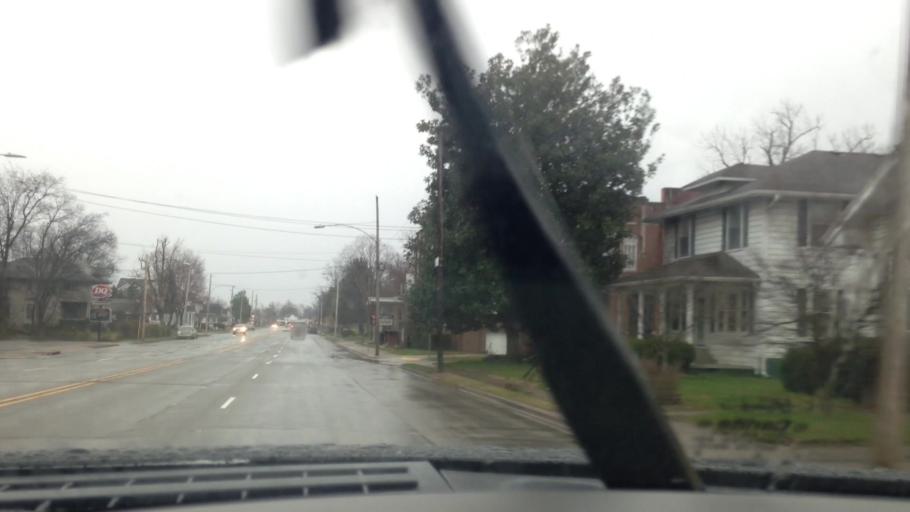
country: US
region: Illinois
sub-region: Massac County
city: Metropolis
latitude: 37.1493
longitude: -88.7287
